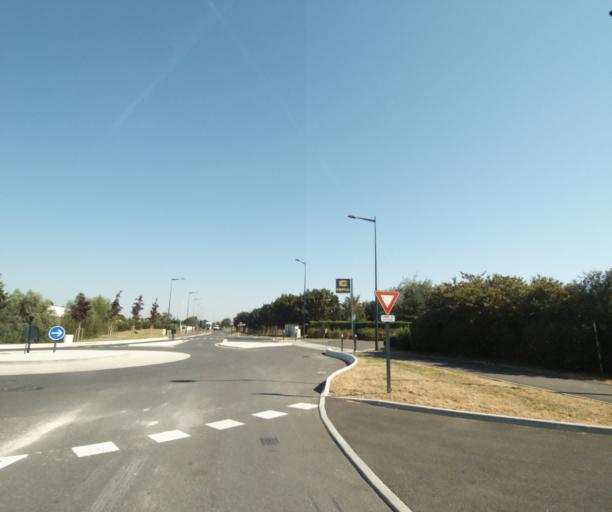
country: FR
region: Ile-de-France
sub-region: Departement de Seine-et-Marne
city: Moissy-Cramayel
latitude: 48.6180
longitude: 2.5812
